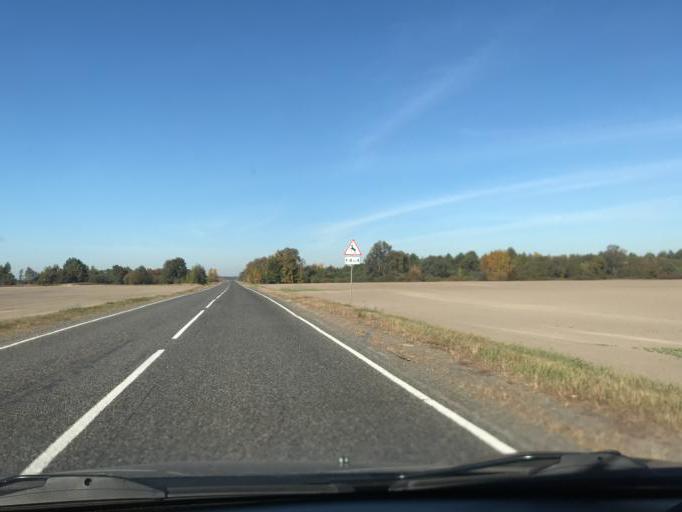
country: UA
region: Chernihiv
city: Lyubech
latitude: 51.6331
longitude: 30.4808
